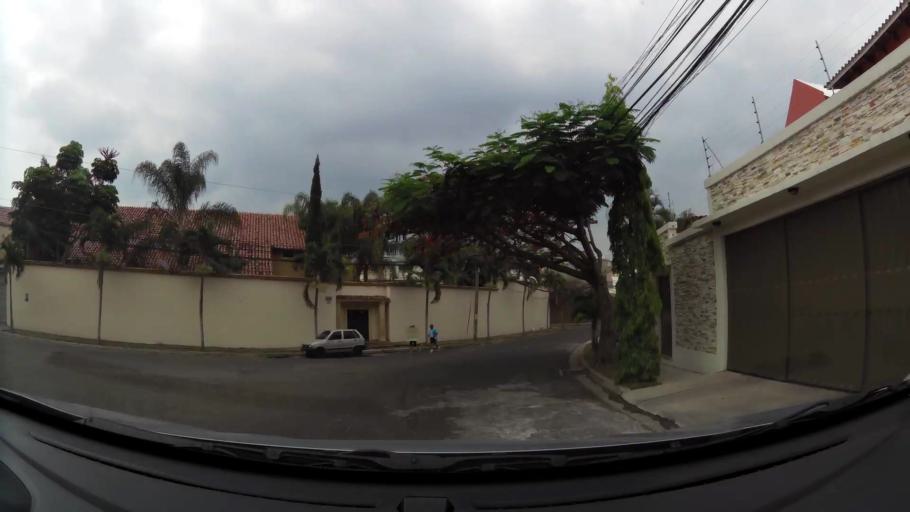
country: HN
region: Francisco Morazan
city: Tegucigalpa
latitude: 14.0934
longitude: -87.1743
